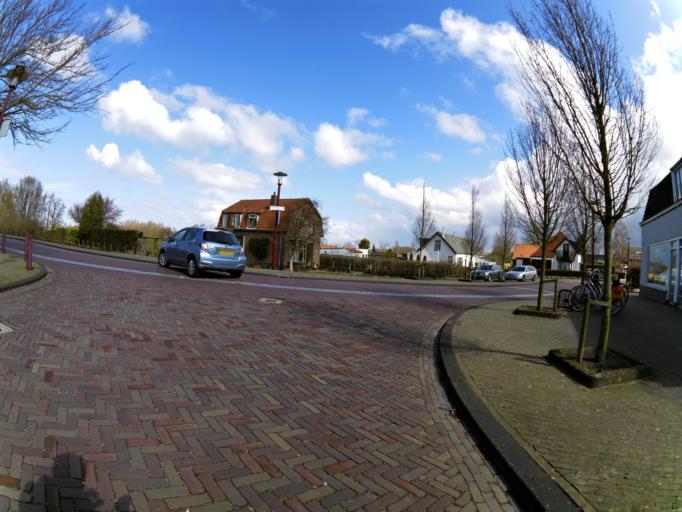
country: NL
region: South Holland
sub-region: Gemeente Hellevoetsluis
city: Nieuw-Helvoet
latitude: 51.8749
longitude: 4.0675
